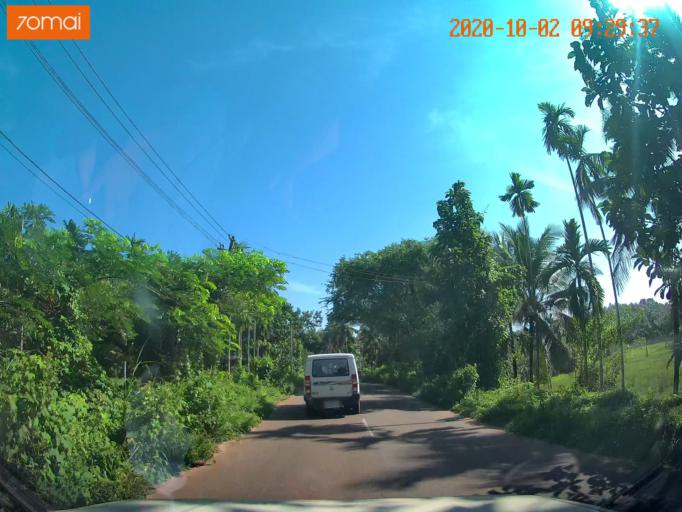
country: IN
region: Kerala
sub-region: Kozhikode
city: Naduvannur
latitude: 11.6142
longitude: 75.7613
